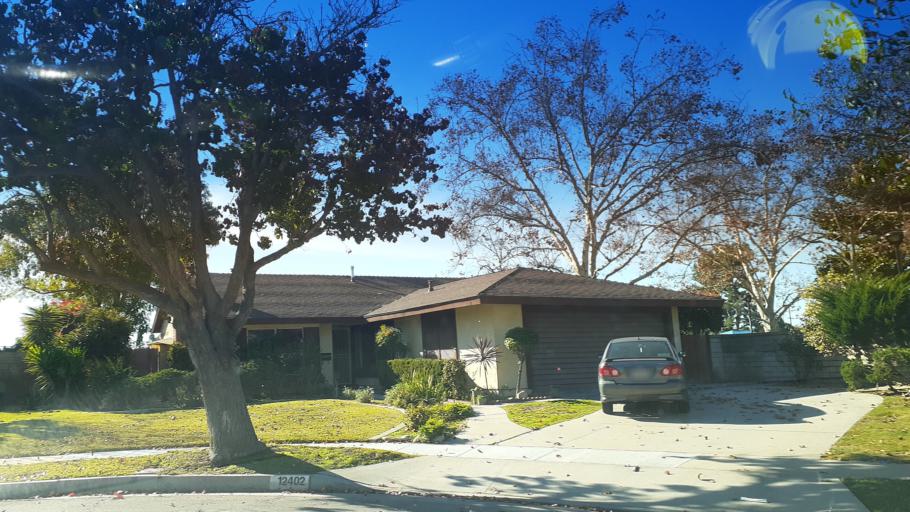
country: US
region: California
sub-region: Los Angeles County
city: Cerritos
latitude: 33.8574
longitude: -118.0676
